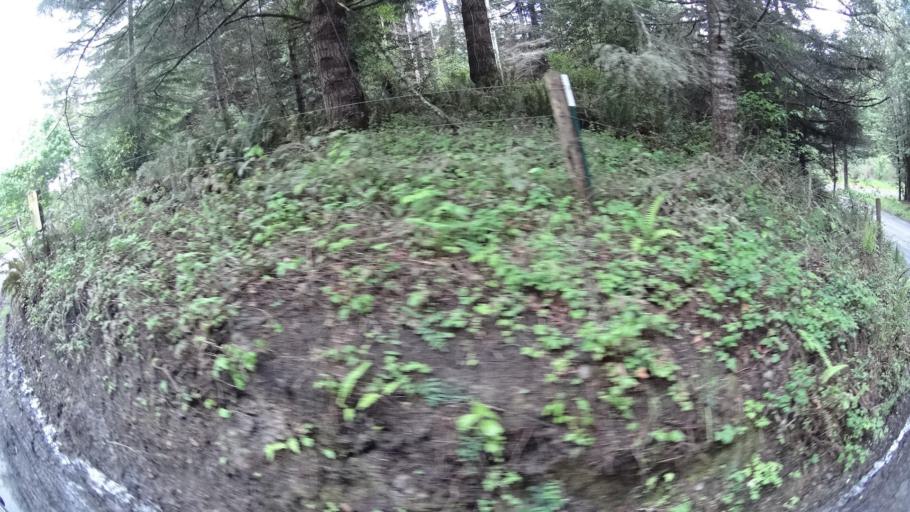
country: US
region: California
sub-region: Humboldt County
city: Blue Lake
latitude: 40.9077
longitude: -123.9746
